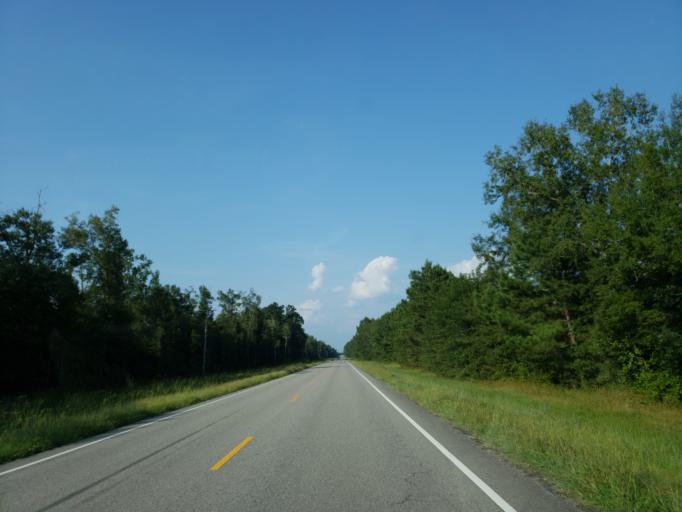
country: US
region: Alabama
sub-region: Sumter County
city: Livingston
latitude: 32.7307
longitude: -88.0607
